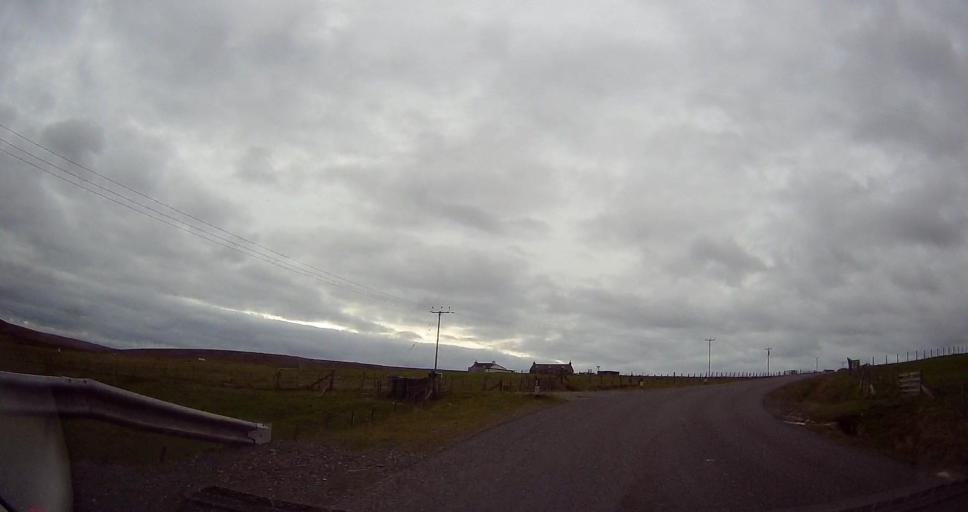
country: GB
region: Scotland
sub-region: Shetland Islands
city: Shetland
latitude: 60.6613
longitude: -1.0496
